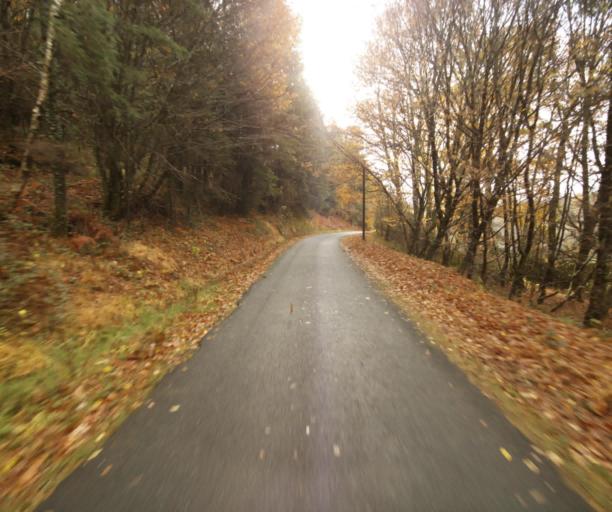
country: FR
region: Limousin
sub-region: Departement de la Correze
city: Cornil
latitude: 45.2069
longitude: 1.6594
